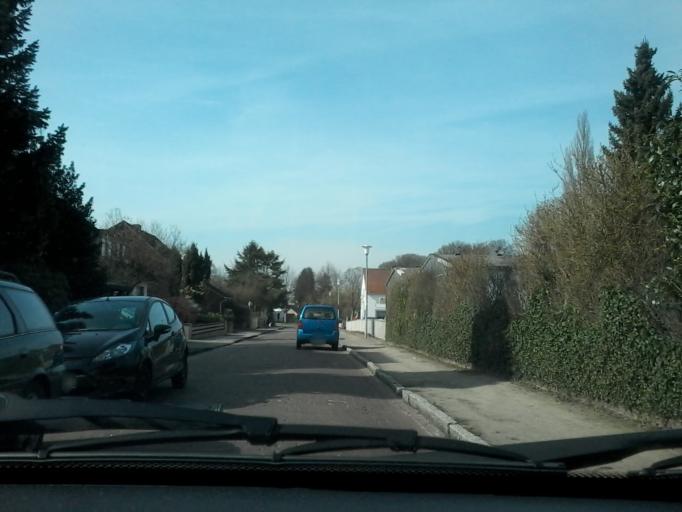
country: DE
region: Lower Saxony
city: Achim
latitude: 53.0143
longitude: 9.0381
